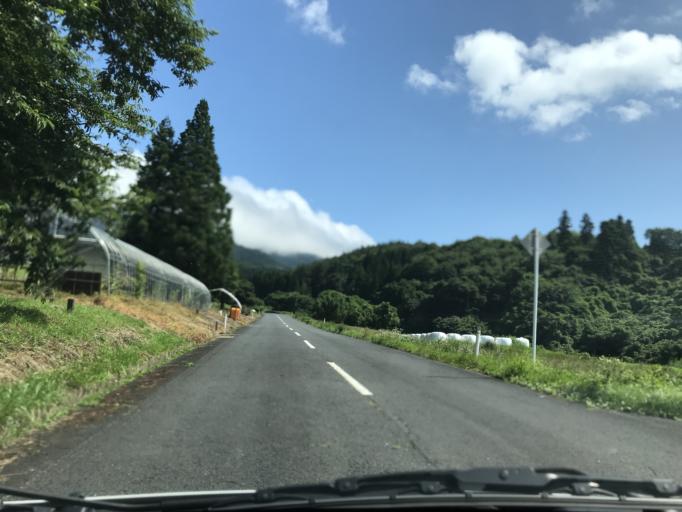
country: JP
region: Iwate
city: Ofunato
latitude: 39.0016
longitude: 141.4259
